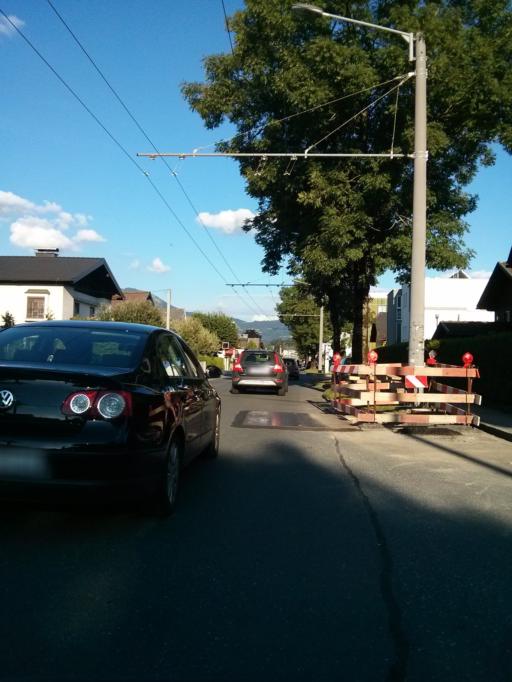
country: AT
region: Salzburg
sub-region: Politischer Bezirk Salzburg-Umgebung
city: Bergheim
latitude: 47.8102
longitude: 13.0092
